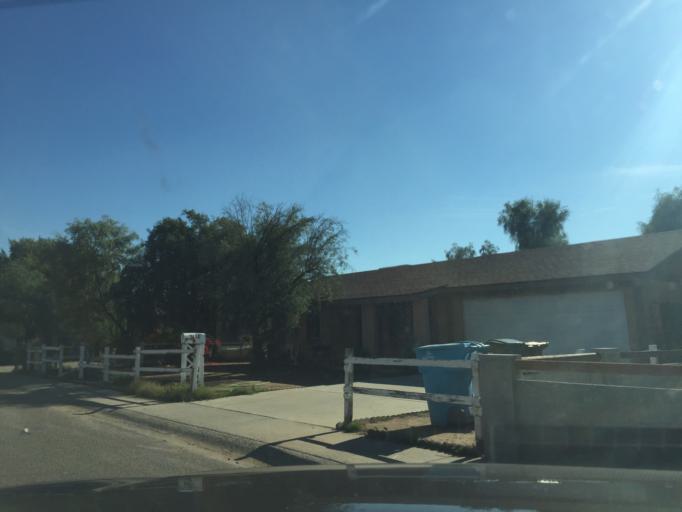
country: US
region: Arizona
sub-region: Maricopa County
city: Tolleson
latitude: 33.4676
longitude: -112.2187
